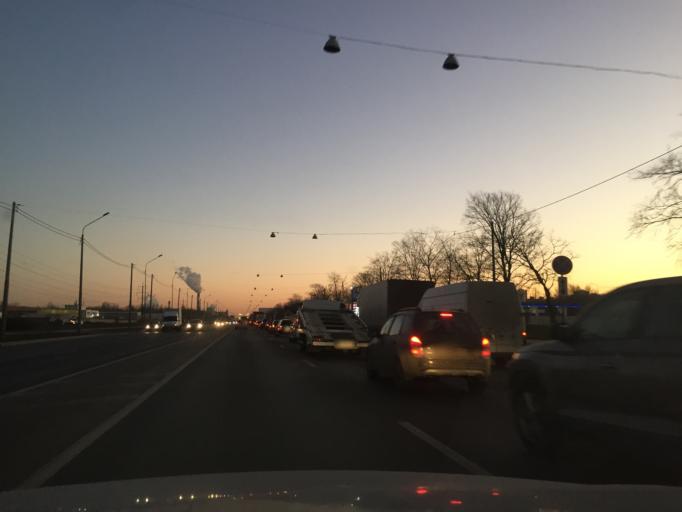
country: RU
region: St.-Petersburg
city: Obukhovo
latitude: 59.8569
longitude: 30.4224
